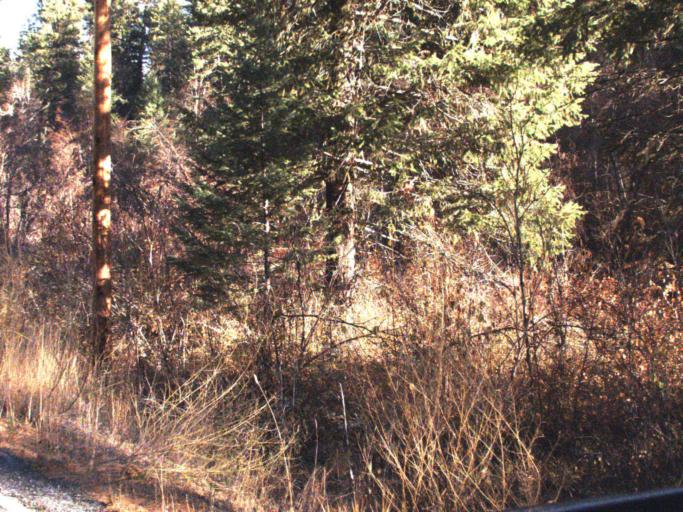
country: US
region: Washington
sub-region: Ferry County
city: Republic
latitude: 48.4079
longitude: -118.7349
